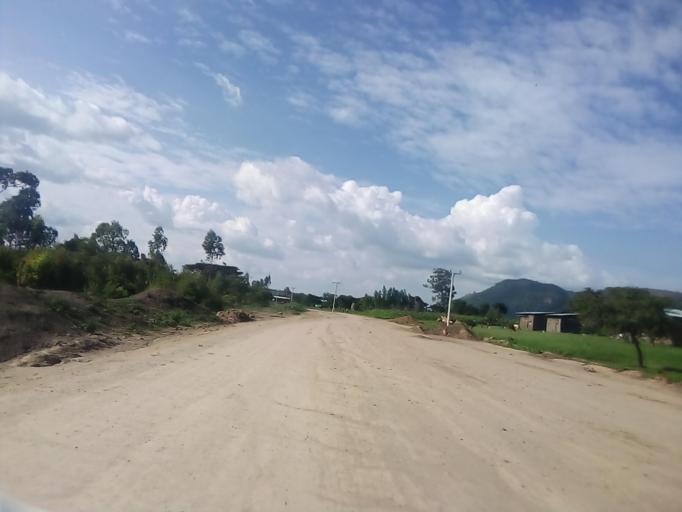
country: ET
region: Southern Nations, Nationalities, and People's Region
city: K'olito
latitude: 7.6126
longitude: 38.0651
